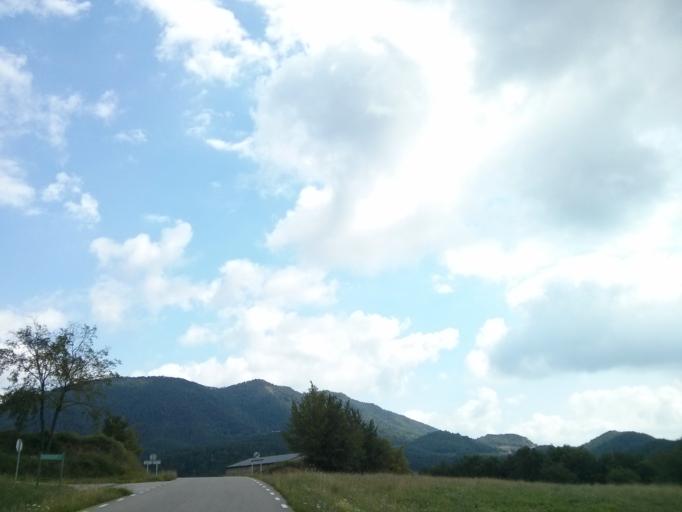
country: ES
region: Catalonia
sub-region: Provincia de Barcelona
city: Borreda
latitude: 42.1363
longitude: 1.9973
